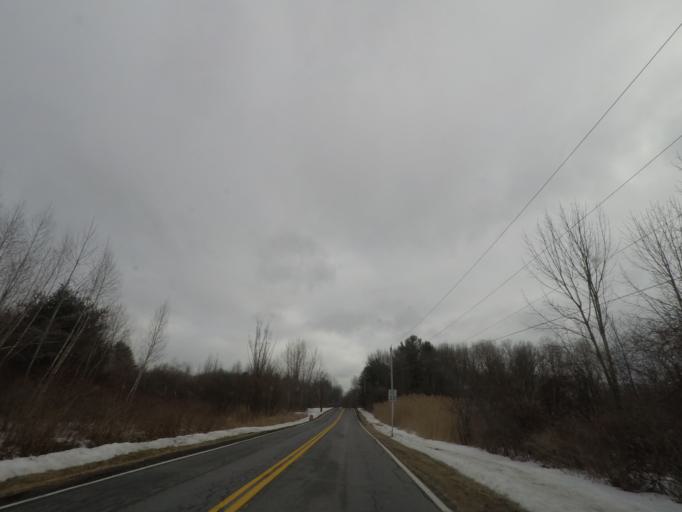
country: US
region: New York
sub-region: Schenectady County
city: Rotterdam
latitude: 42.7398
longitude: -73.9653
